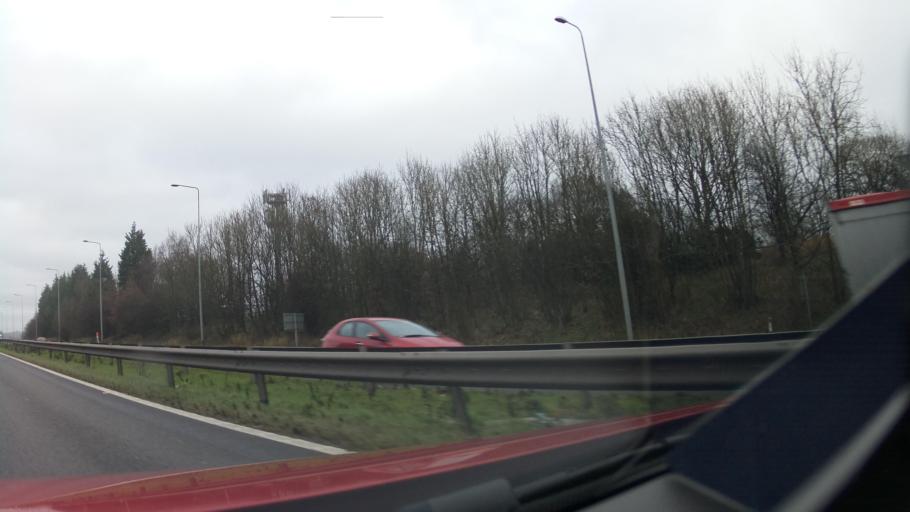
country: GB
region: England
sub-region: Borough of Wigan
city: Shevington
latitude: 53.5957
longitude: -2.6933
